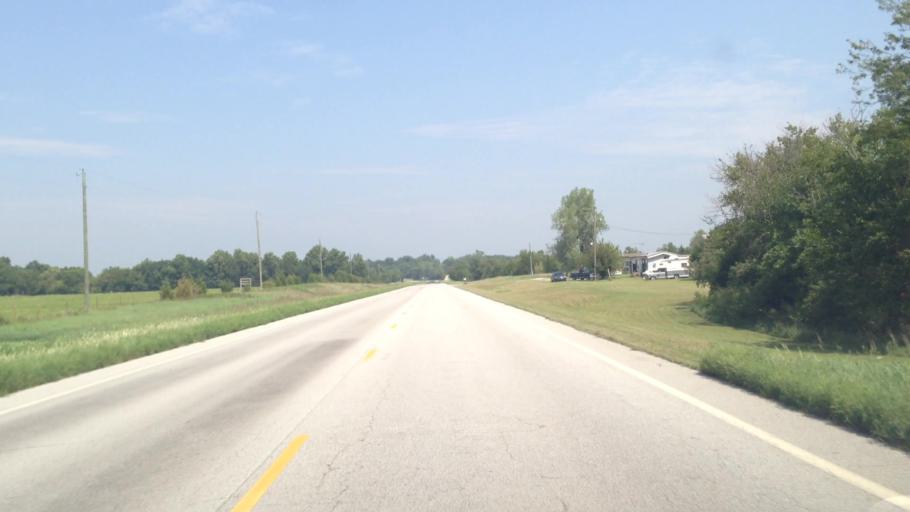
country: US
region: Kansas
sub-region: Labette County
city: Oswego
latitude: 37.1383
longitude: -95.1034
